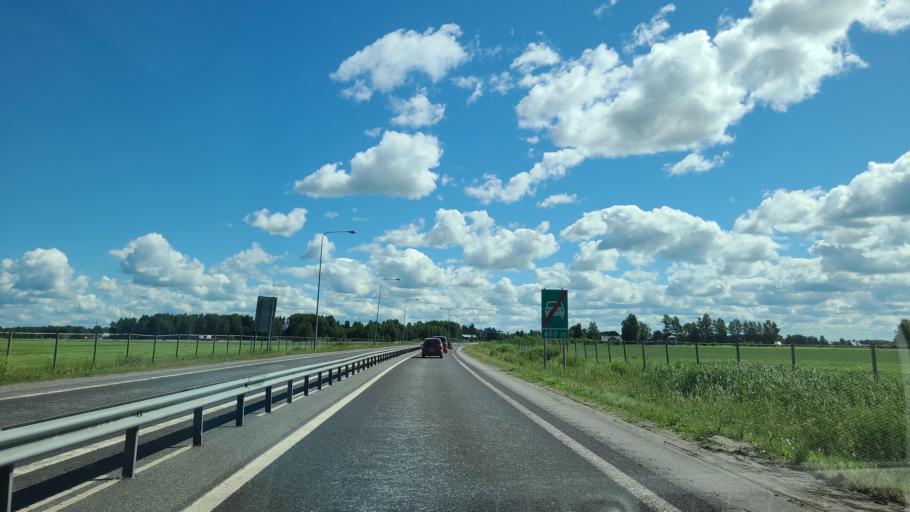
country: FI
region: Ostrobothnia
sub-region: Vaasa
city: Ristinummi
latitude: 63.0250
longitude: 21.7840
